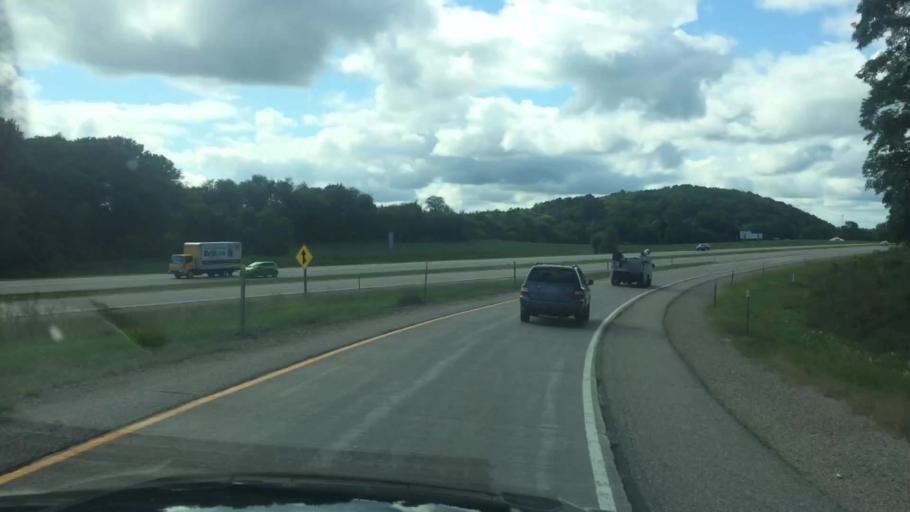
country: US
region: Wisconsin
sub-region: Waupaca County
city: Waupaca
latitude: 44.3410
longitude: -89.0701
